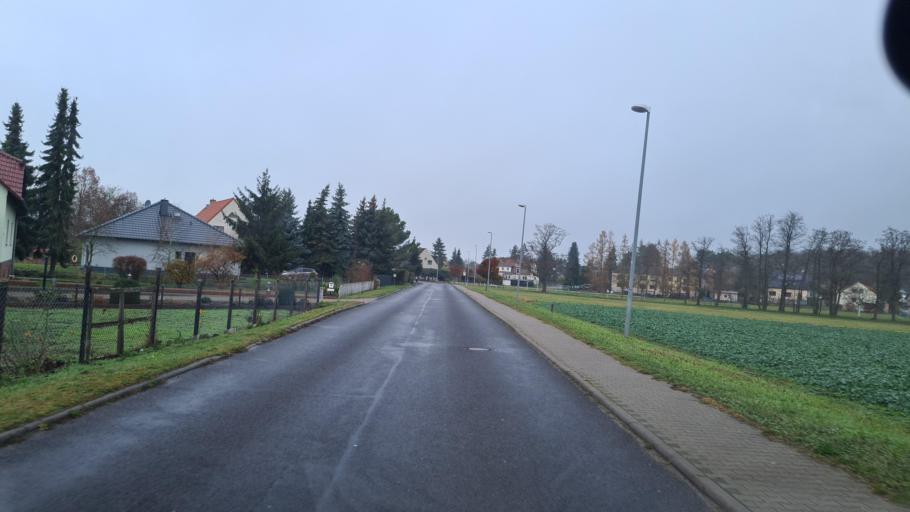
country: DE
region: Brandenburg
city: Roskow
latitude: 52.4137
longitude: 12.7264
